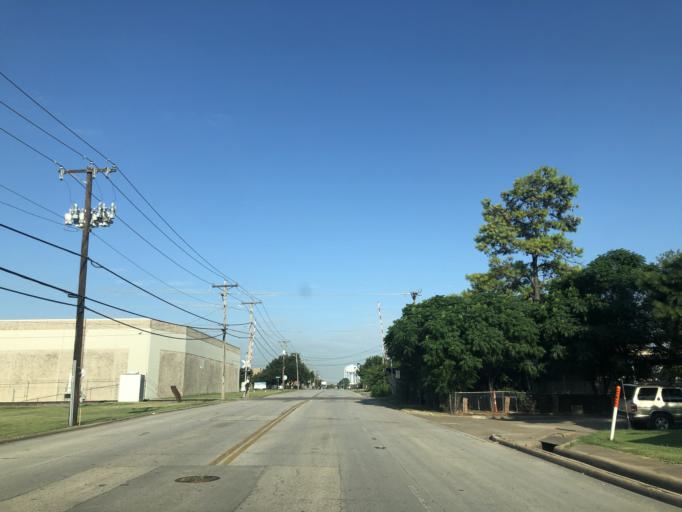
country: US
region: Texas
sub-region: Dallas County
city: Grand Prairie
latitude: 32.7351
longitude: -97.0411
